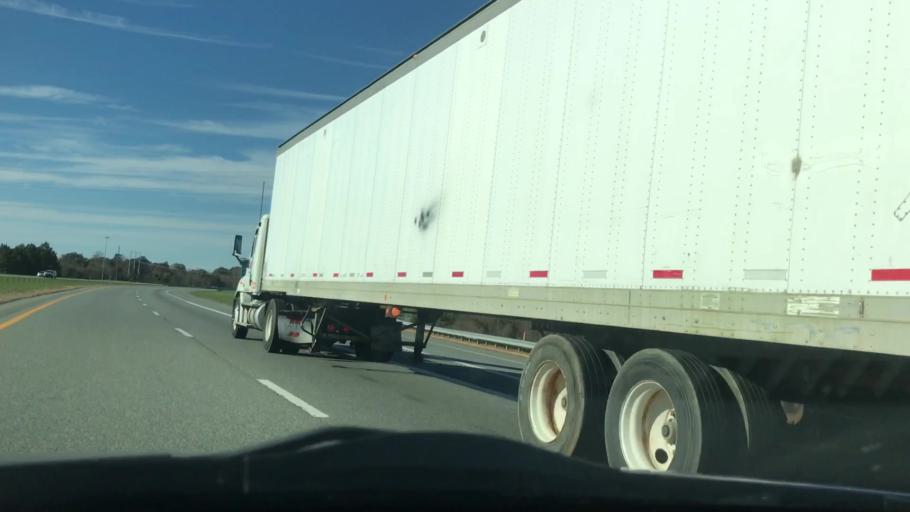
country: US
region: North Carolina
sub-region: Randolph County
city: Archdale
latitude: 35.9424
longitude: -79.9683
